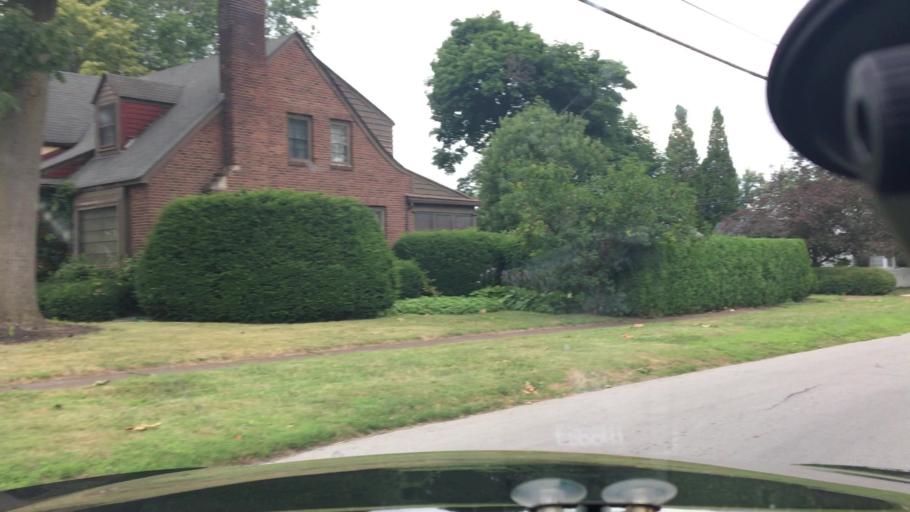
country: US
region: New York
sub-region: Erie County
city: Lackawanna
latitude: 42.8373
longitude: -78.8123
